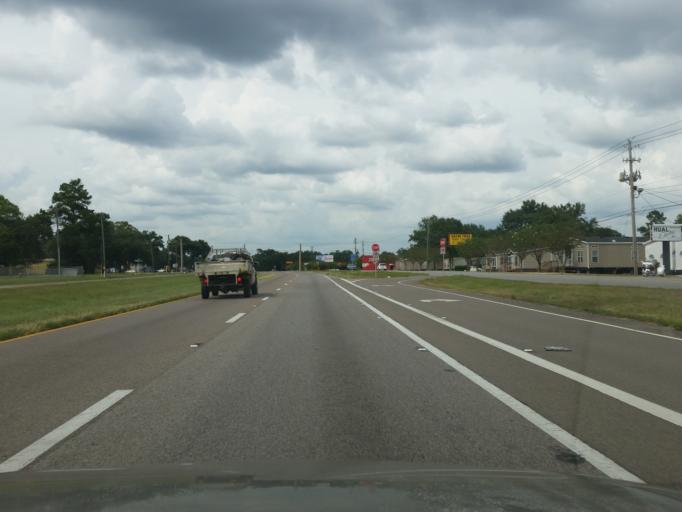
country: US
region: Florida
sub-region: Escambia County
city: Gonzalez
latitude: 30.5604
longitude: -87.2860
